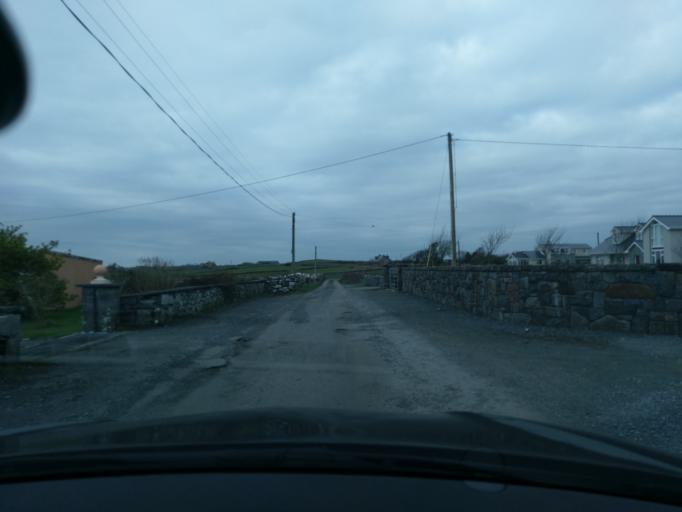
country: IE
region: Connaught
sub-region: County Galway
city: Oranmore
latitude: 53.2007
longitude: -8.9220
